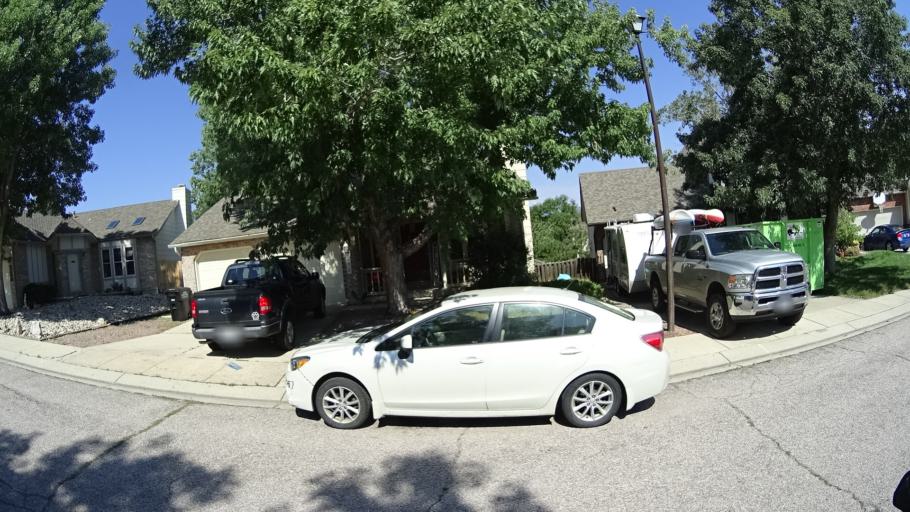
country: US
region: Colorado
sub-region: El Paso County
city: Air Force Academy
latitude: 38.9482
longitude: -104.7892
